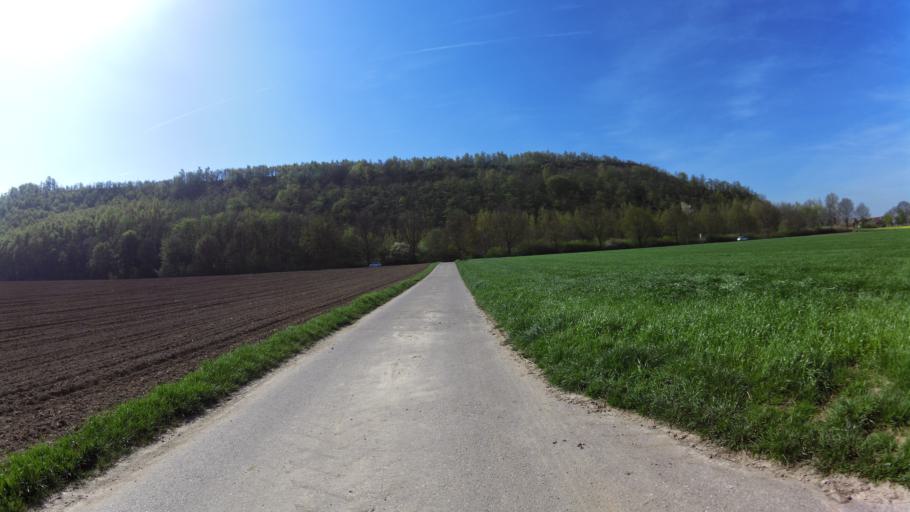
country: DE
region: North Rhine-Westphalia
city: Baesweiler
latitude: 50.9138
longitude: 6.1567
